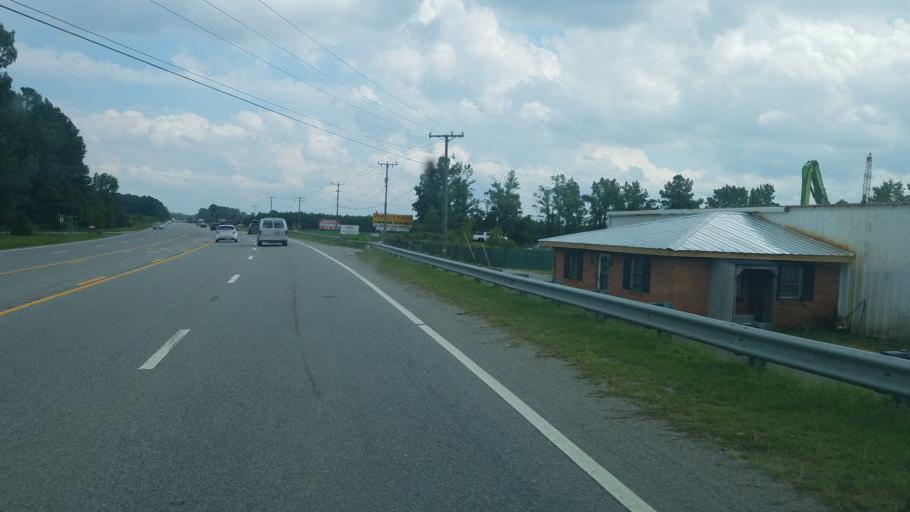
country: US
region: North Carolina
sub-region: Currituck County
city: Moyock
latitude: 36.4788
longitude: -76.1292
